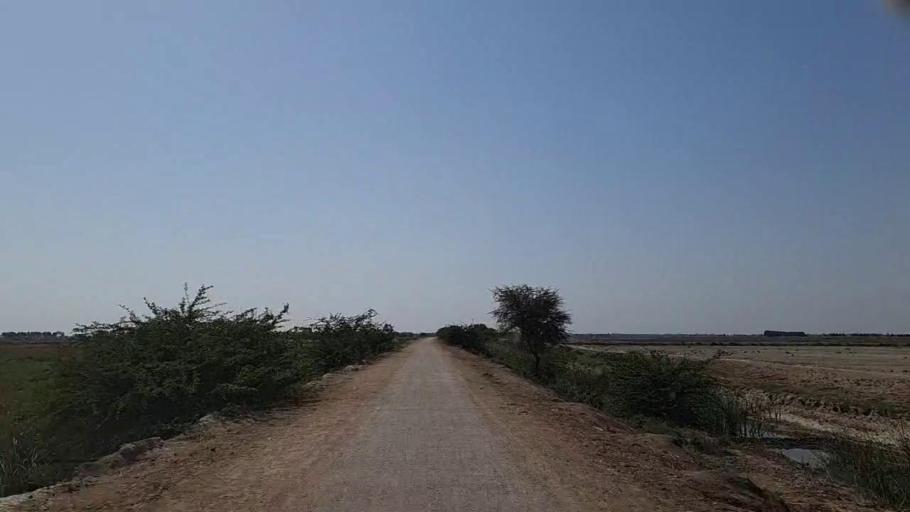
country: PK
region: Sindh
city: Mirpur Batoro
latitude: 24.6765
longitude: 68.3050
